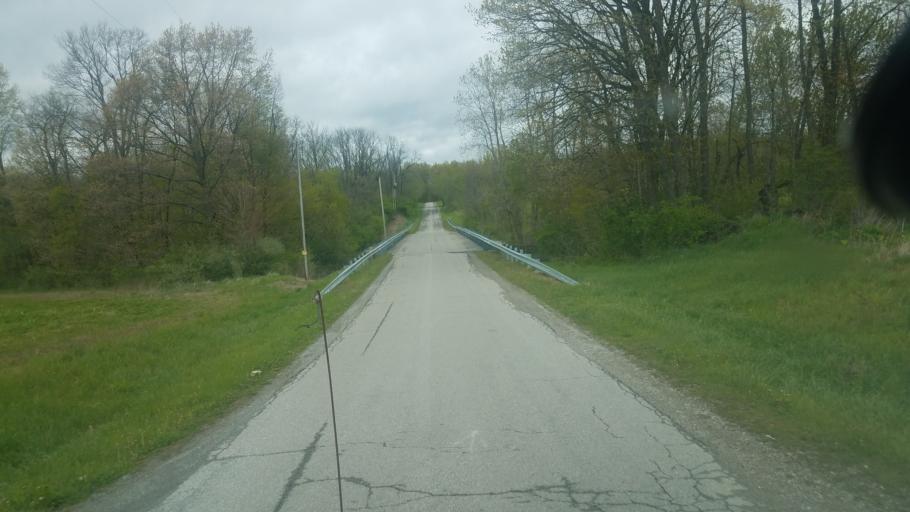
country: US
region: Ohio
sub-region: Crawford County
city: Bucyrus
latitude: 40.7610
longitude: -83.0736
